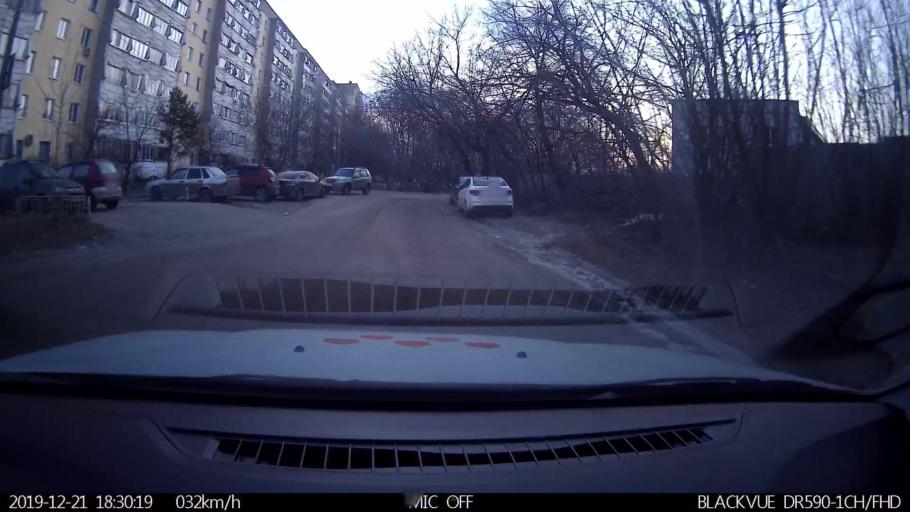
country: RU
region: Nizjnij Novgorod
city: Nizhniy Novgorod
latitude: 56.3356
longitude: 43.9155
